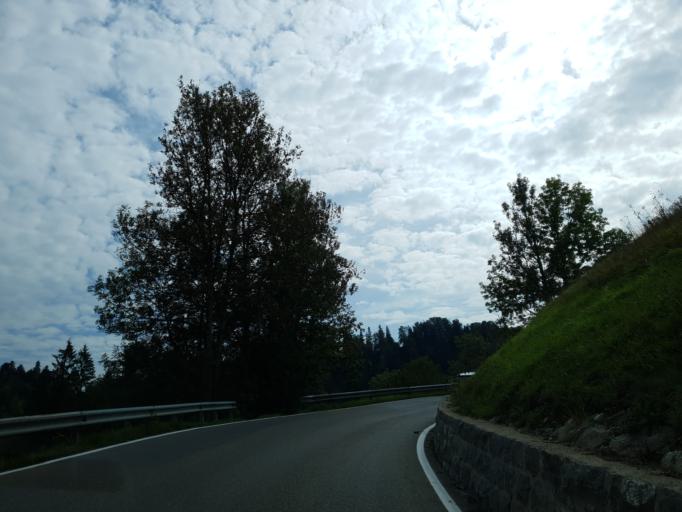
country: AT
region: Vorarlberg
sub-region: Politischer Bezirk Bregenz
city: Krumbach
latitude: 47.4968
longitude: 9.9151
